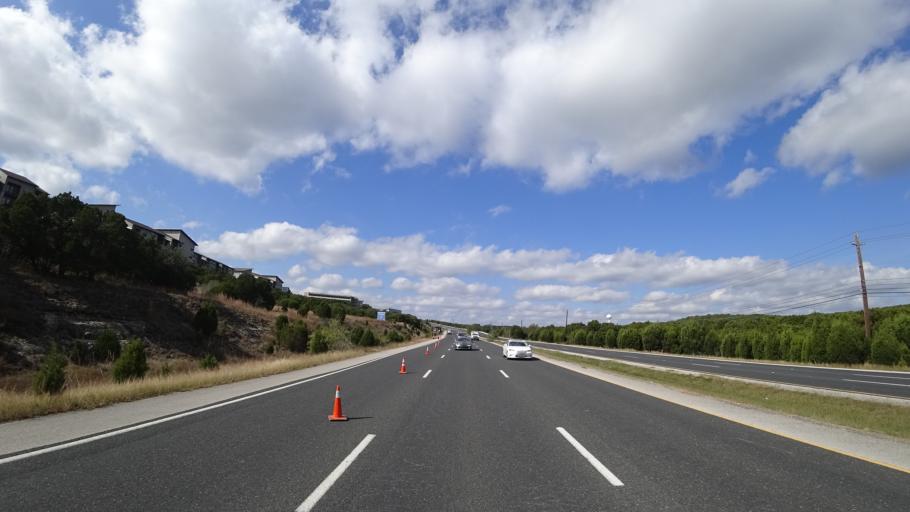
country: US
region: Texas
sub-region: Travis County
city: Barton Creek
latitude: 30.2504
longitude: -97.8551
